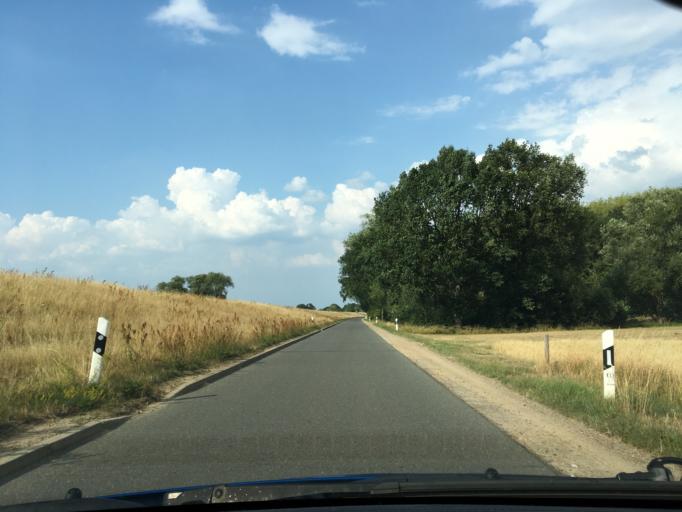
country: DE
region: Lower Saxony
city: Damnatz
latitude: 53.1530
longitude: 11.1245
